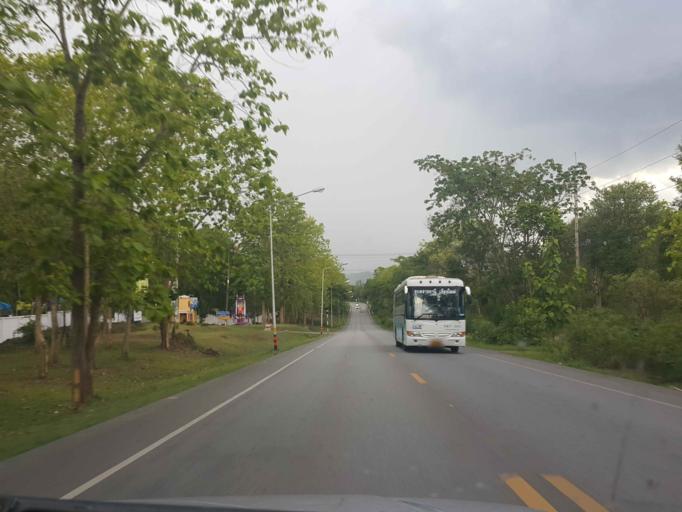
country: TH
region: Phrae
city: Den Chai
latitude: 17.9742
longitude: 100.0411
